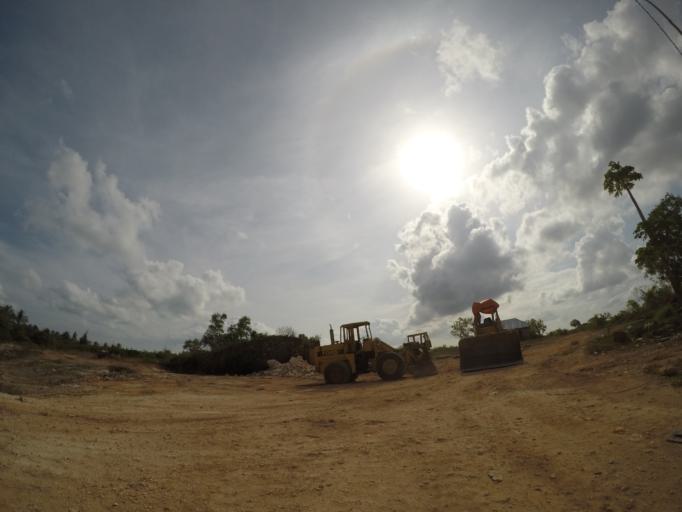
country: TZ
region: Zanzibar Central/South
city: Koani
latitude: -6.2320
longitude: 39.3213
